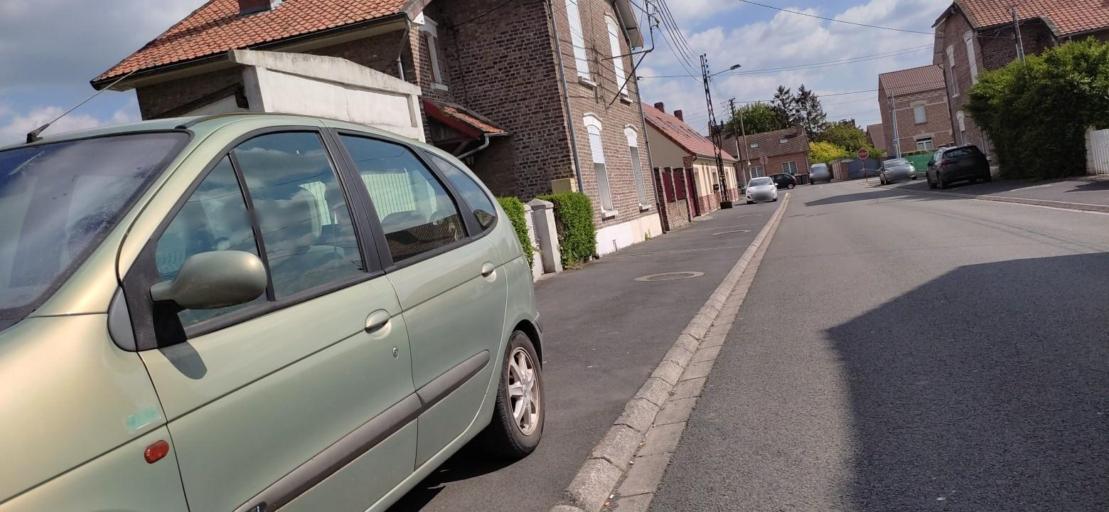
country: FR
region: Nord-Pas-de-Calais
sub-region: Departement du Pas-de-Calais
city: Biache-Saint-Vaast
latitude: 50.3136
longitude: 2.9427
